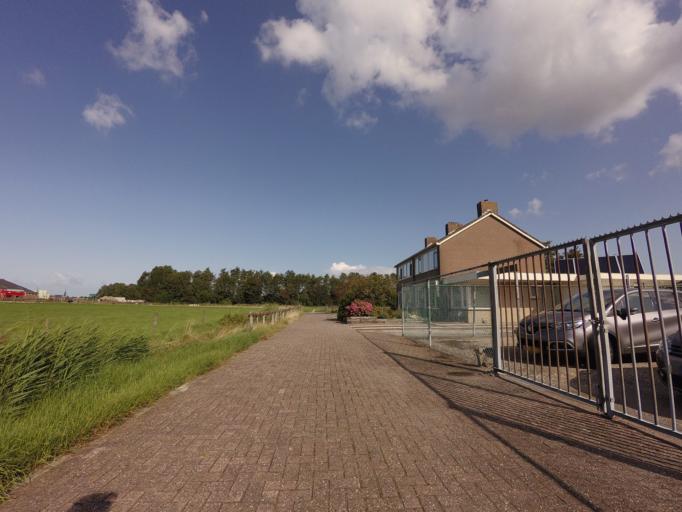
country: NL
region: Friesland
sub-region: Gemeente Franekeradeel
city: Tzummarum
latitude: 53.2378
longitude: 5.5393
